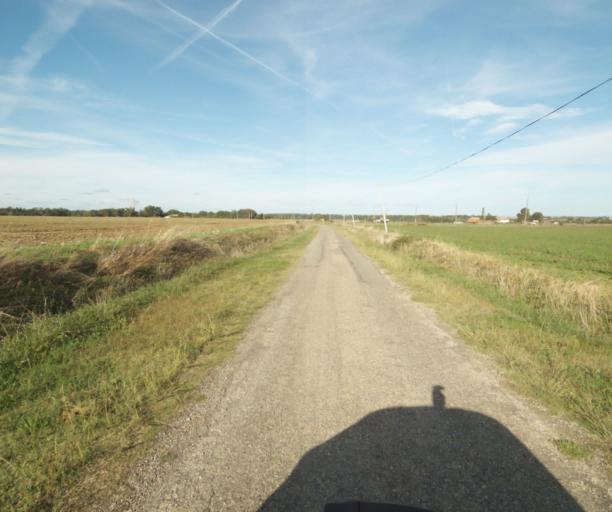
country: FR
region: Midi-Pyrenees
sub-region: Departement du Tarn-et-Garonne
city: Finhan
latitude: 43.9259
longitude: 1.1383
